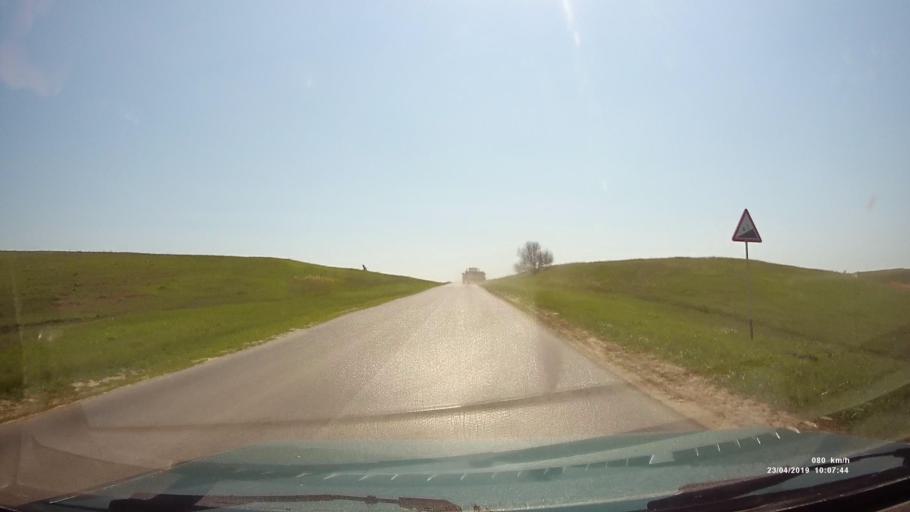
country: RU
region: Rostov
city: Sovetskoye
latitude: 46.7229
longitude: 42.2582
